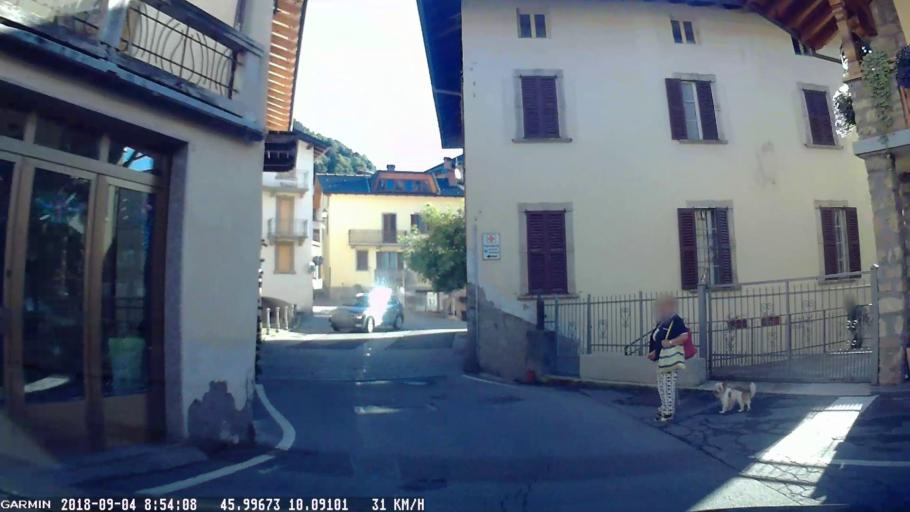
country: IT
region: Lombardy
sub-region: Provincia di Bergamo
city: Vilminore
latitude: 45.9984
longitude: 10.0972
